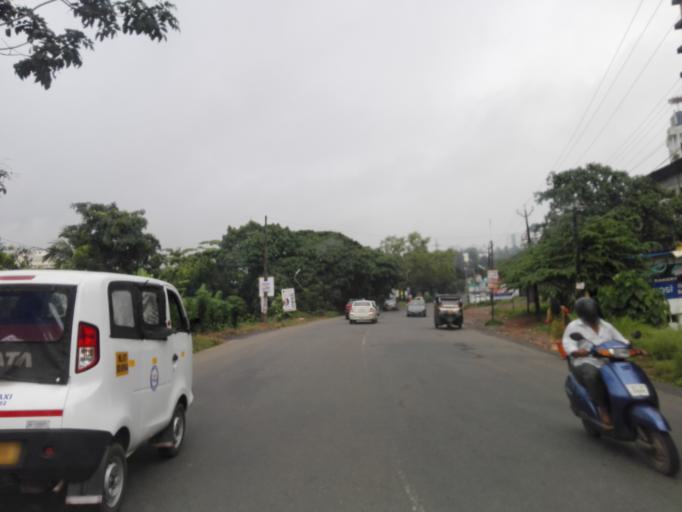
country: IN
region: Kerala
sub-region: Ernakulam
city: Elur
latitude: 10.0240
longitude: 76.3387
